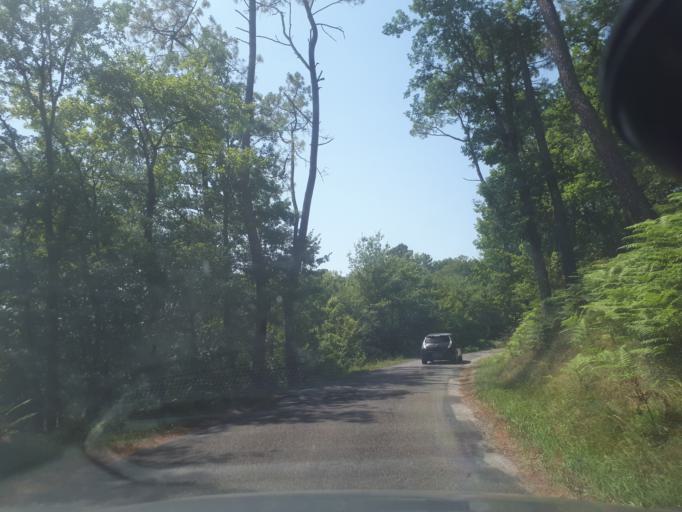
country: FR
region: Midi-Pyrenees
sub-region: Departement du Lot
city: Gourdon
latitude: 44.7472
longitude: 1.3342
